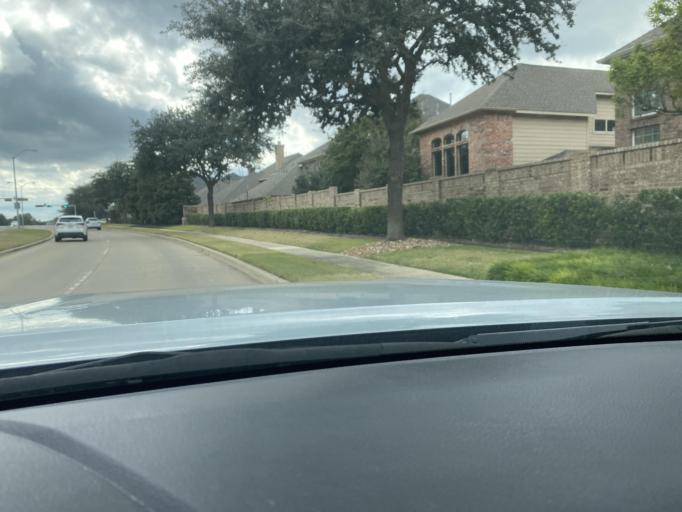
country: US
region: Texas
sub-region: Dallas County
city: Addison
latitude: 33.0371
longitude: -96.7899
